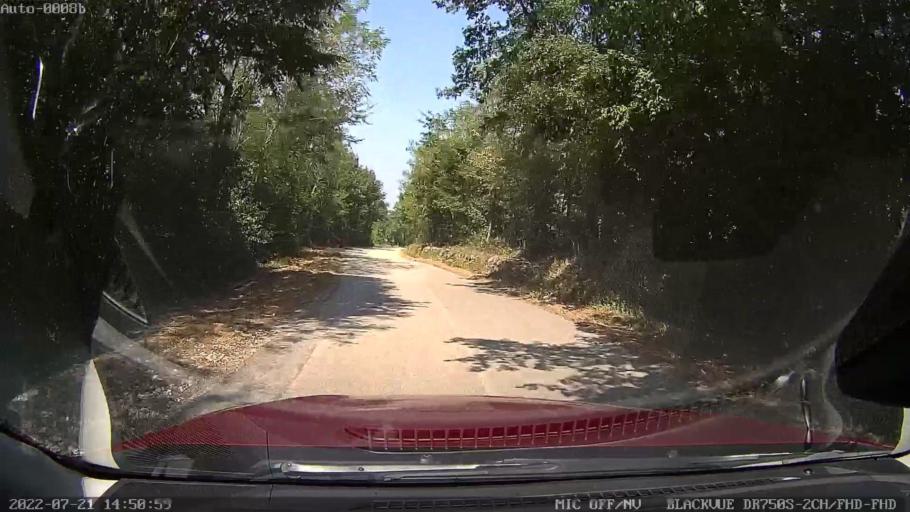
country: HR
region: Istarska
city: Pazin
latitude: 45.1651
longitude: 13.9188
